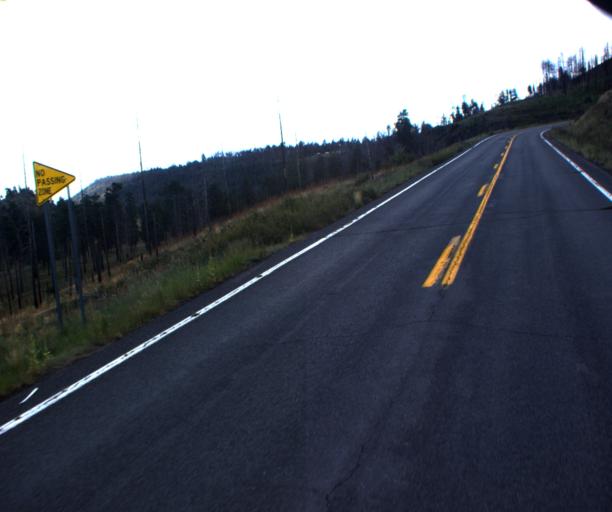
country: US
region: Arizona
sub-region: Apache County
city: Eagar
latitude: 34.0465
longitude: -109.3589
